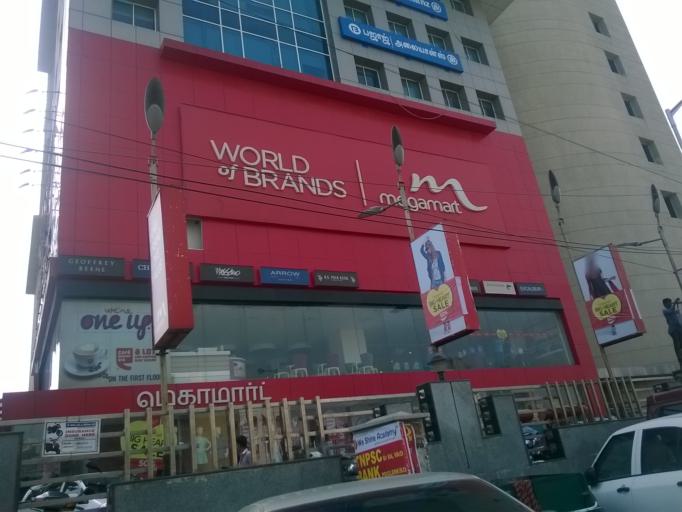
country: IN
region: Tamil Nadu
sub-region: Chennai
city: Chetput
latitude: 13.0770
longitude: 80.2090
